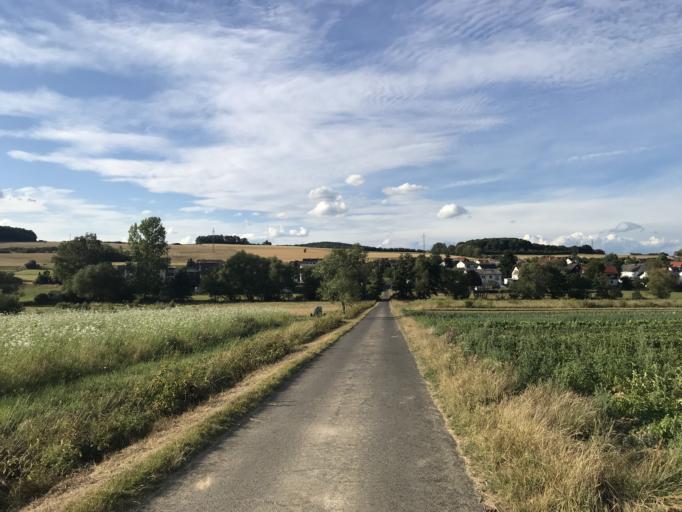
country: DE
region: Hesse
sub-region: Regierungsbezirk Giessen
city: Lohra
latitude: 50.6849
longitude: 8.6019
